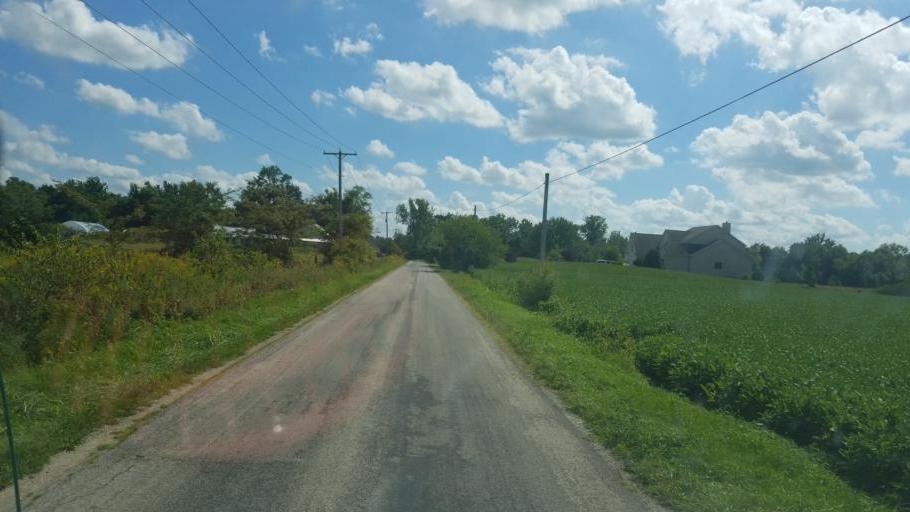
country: US
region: Ohio
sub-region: Union County
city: Richwood
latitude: 40.3439
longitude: -83.2438
